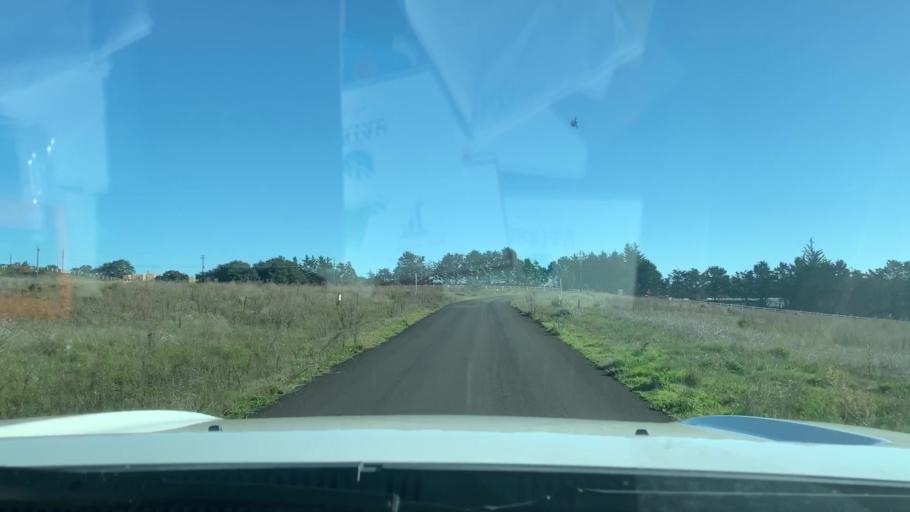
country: US
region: California
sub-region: San Luis Obispo County
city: Callender
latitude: 35.0655
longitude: -120.5633
